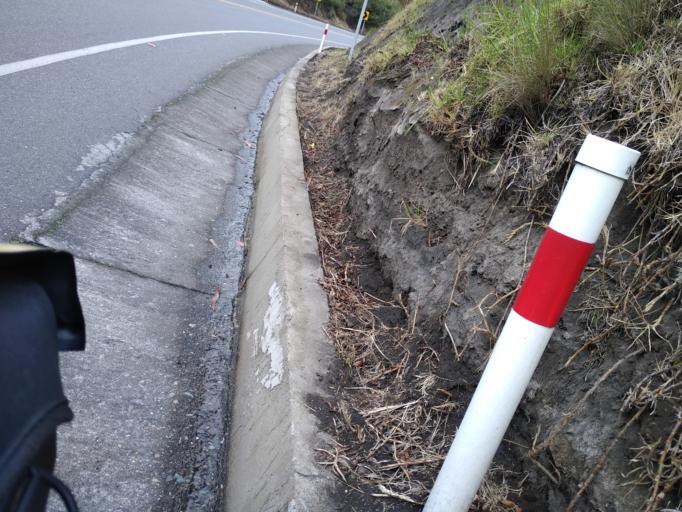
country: EC
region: Tungurahua
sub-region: Canton Quero
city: Quero
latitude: -1.4947
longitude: -78.5254
